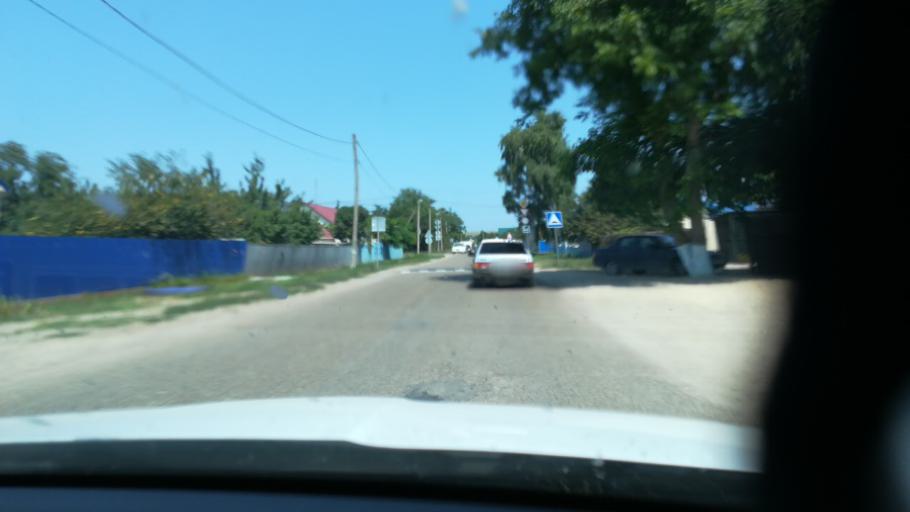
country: RU
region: Krasnodarskiy
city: Starotitarovskaya
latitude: 45.2053
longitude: 37.1470
